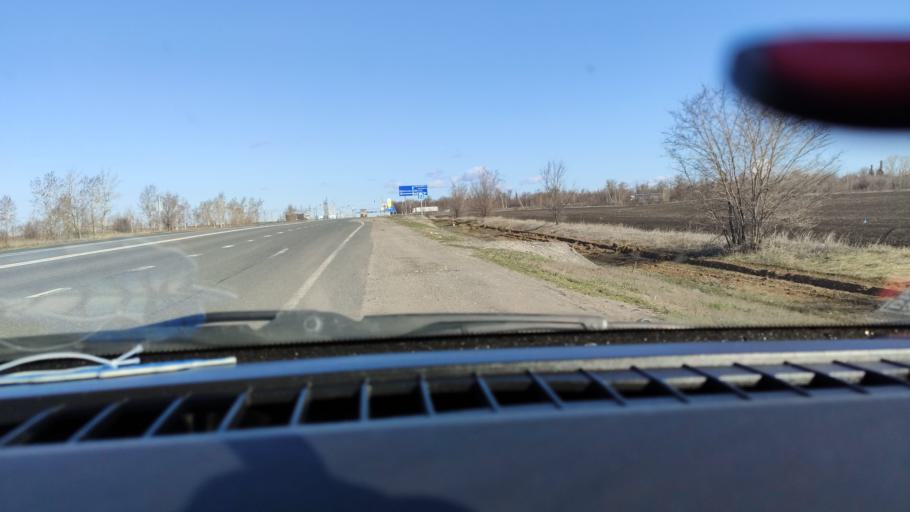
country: RU
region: Samara
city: Syzran'
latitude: 53.2073
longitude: 48.5083
